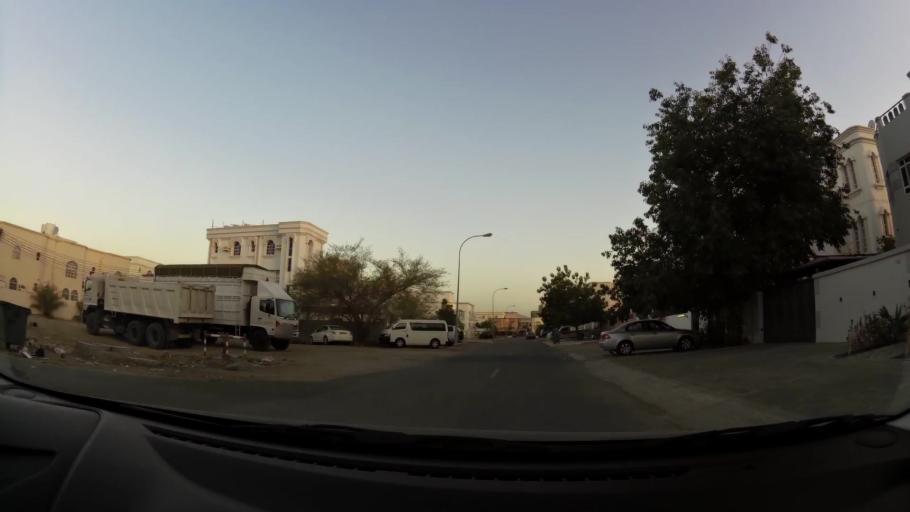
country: OM
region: Muhafazat Masqat
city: As Sib al Jadidah
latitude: 23.5964
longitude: 58.2341
